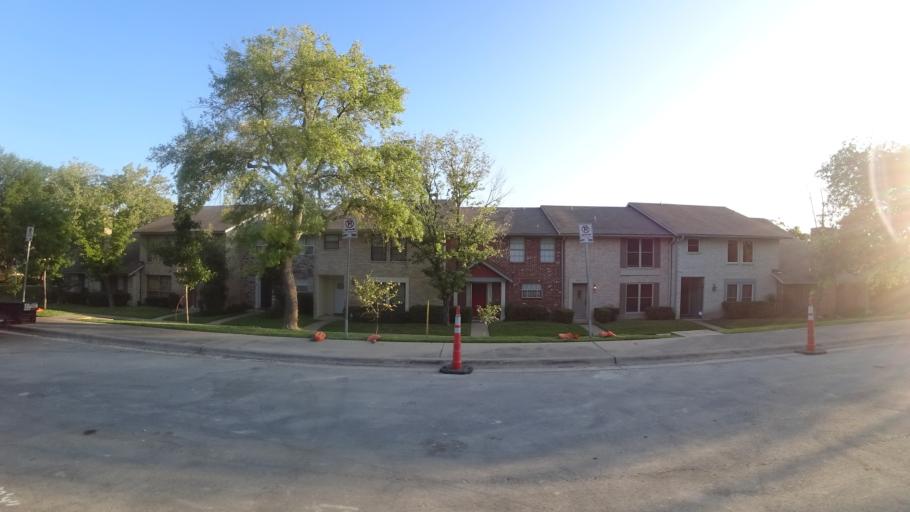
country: US
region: Texas
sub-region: Travis County
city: Austin
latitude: 30.3246
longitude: -97.6821
